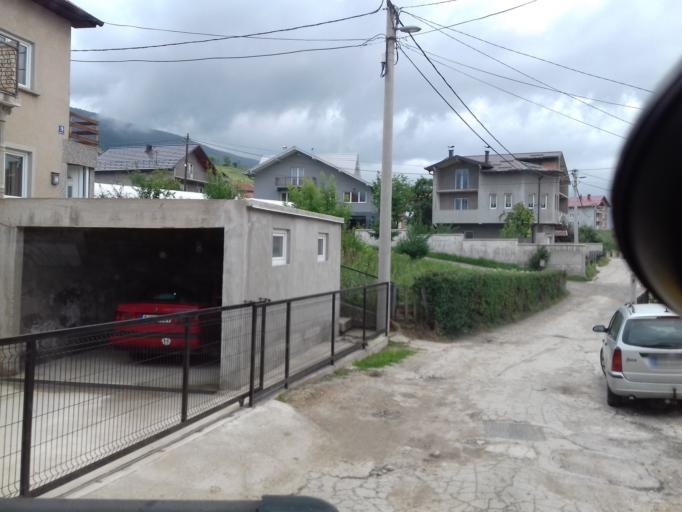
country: BA
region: Federation of Bosnia and Herzegovina
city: Zenica
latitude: 44.1978
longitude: 17.9319
